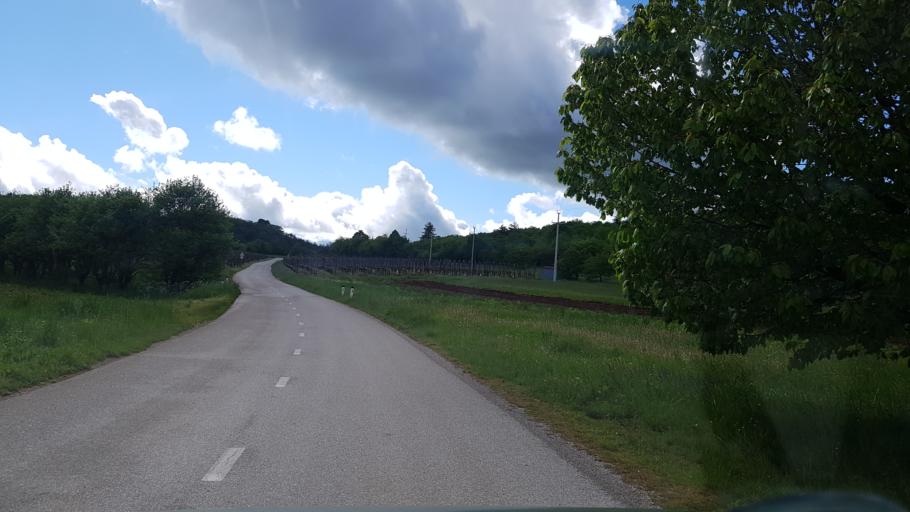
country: SI
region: Nova Gorica
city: Prvacina
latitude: 45.8477
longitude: 13.7005
